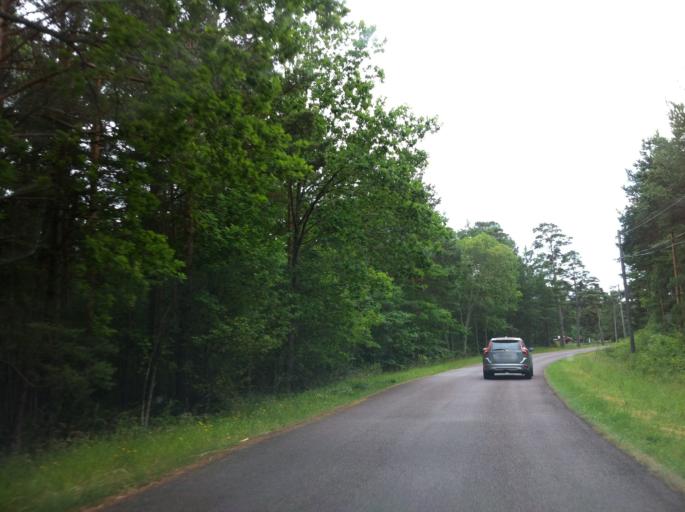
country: SE
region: Kalmar
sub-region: Vasterviks Kommun
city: Vaestervik
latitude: 57.3652
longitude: 17.0703
